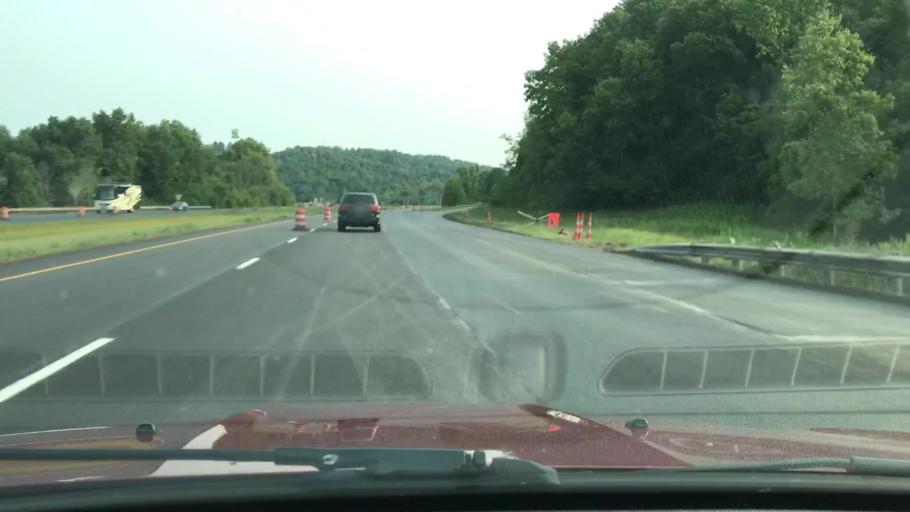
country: US
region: Ohio
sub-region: Guernsey County
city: Cambridge
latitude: 40.1409
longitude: -81.5518
